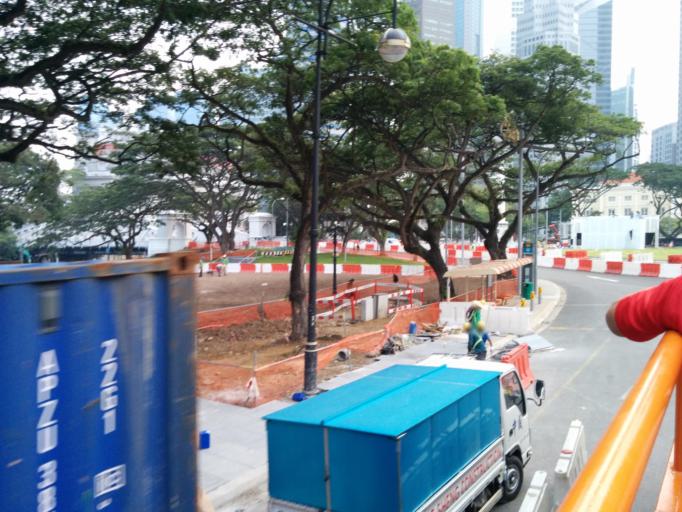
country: SG
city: Singapore
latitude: 1.2886
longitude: 103.8527
